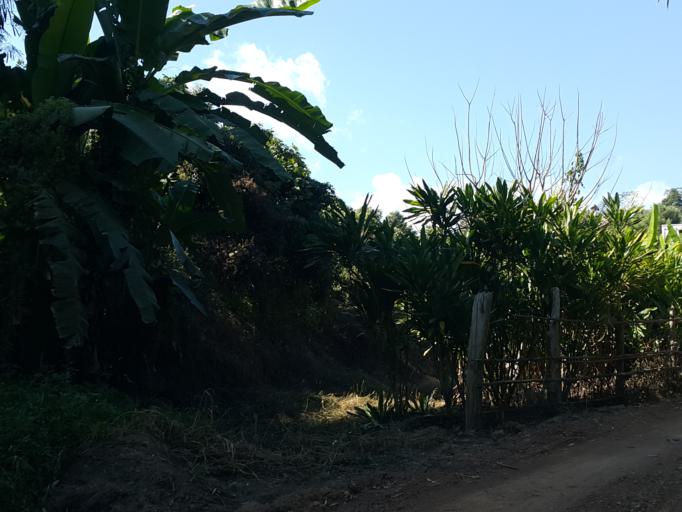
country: TH
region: Chiang Mai
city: Mae Taeng
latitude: 18.9579
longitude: 98.9068
